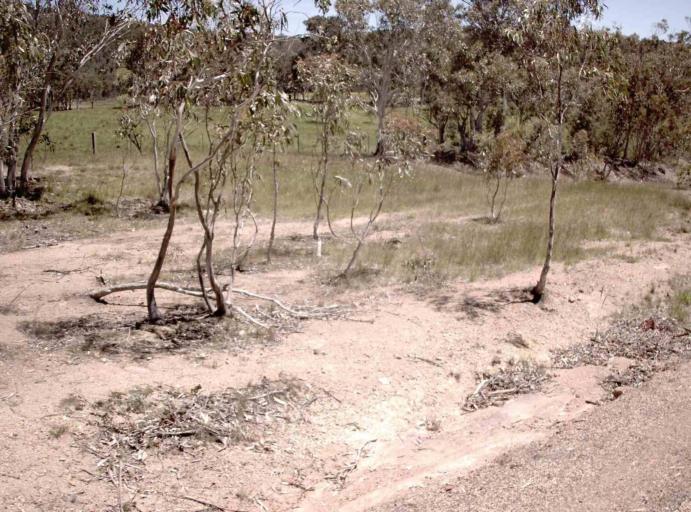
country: AU
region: New South Wales
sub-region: Snowy River
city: Jindabyne
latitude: -37.0715
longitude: 148.2604
